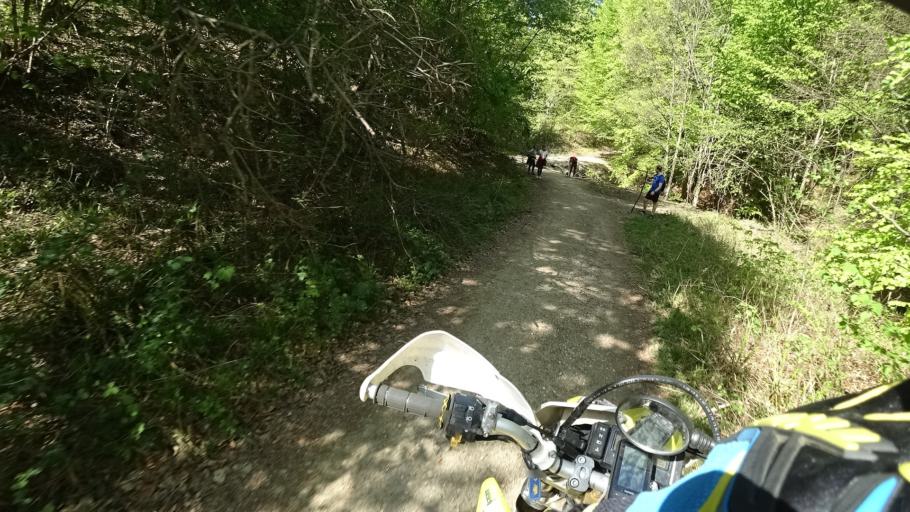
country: HR
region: Zagrebacka
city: Jablanovec
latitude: 45.8680
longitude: 15.8969
